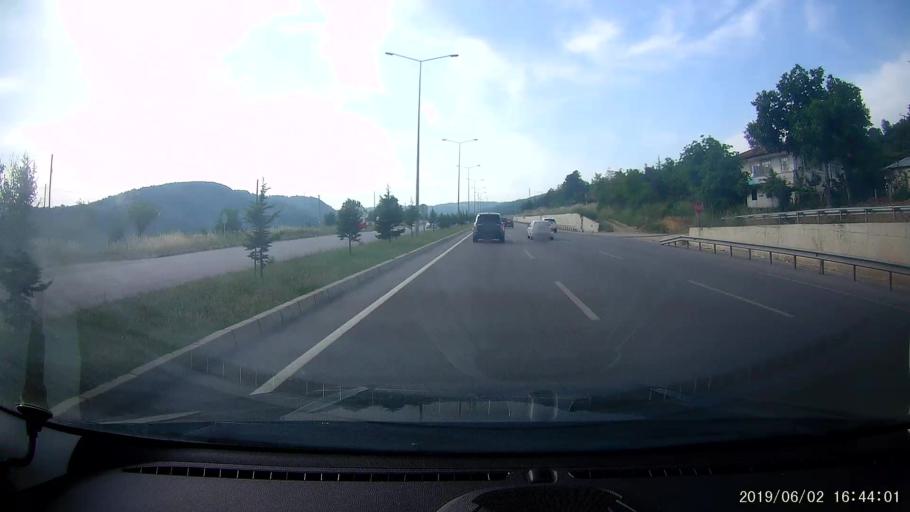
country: TR
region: Samsun
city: Kavak
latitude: 41.1441
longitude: 36.1169
